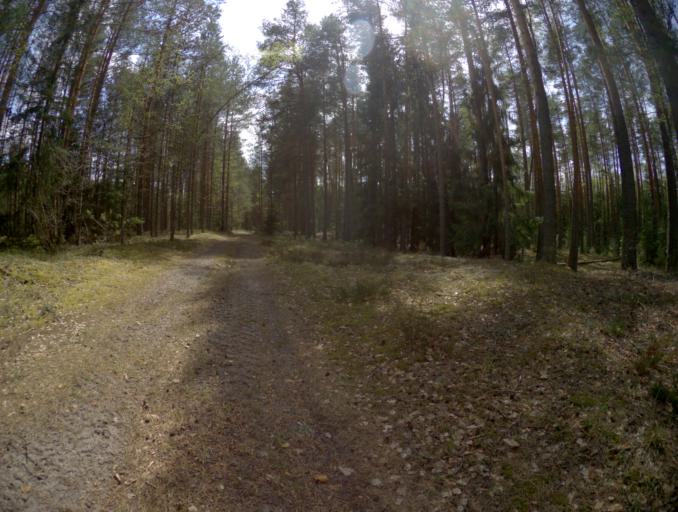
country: RU
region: Vladimir
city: Golovino
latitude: 55.8923
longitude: 40.3880
